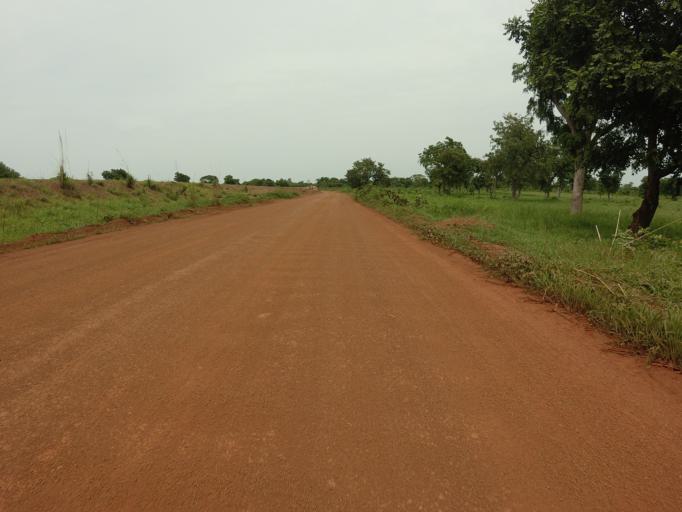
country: GH
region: Northern
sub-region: Yendi
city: Yendi
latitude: 8.9830
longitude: -0.0162
